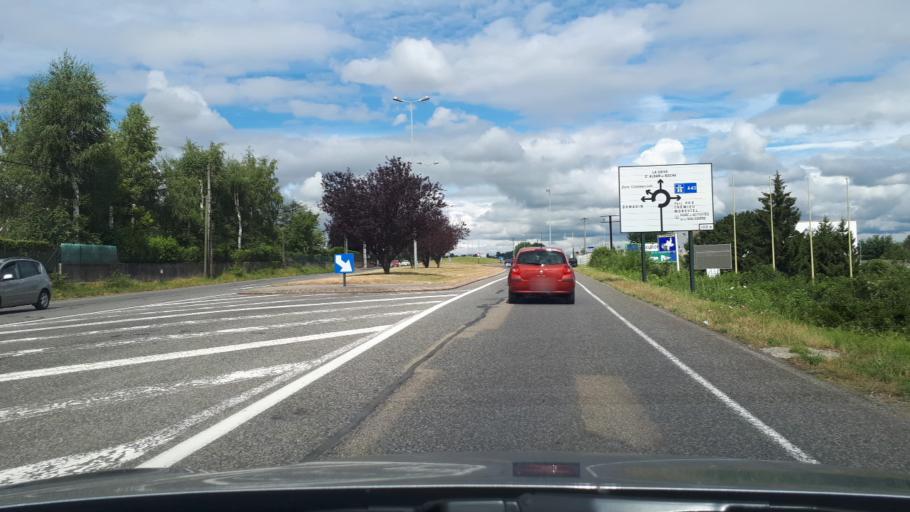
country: FR
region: Rhone-Alpes
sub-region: Departement de l'Isere
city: Domarin
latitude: 45.5885
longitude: 5.2489
